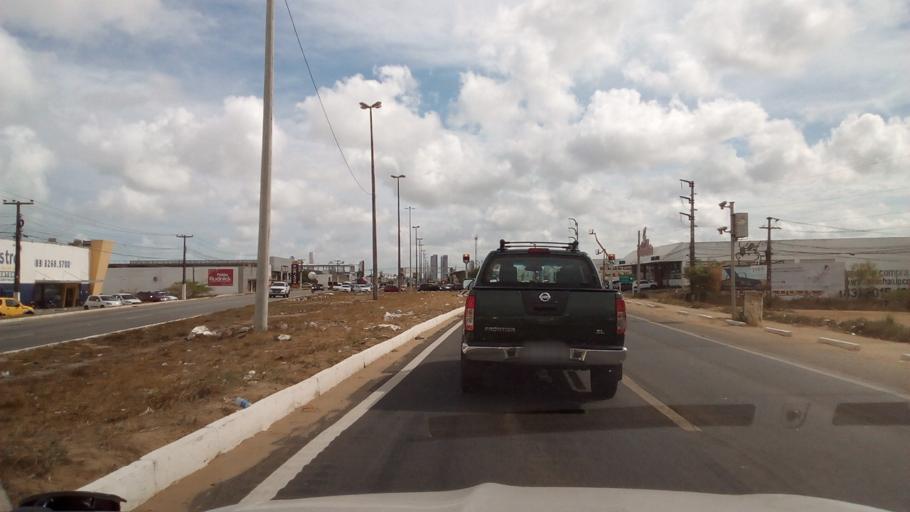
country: BR
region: Paraiba
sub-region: Joao Pessoa
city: Joao Pessoa
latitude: -7.0719
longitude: -34.8497
